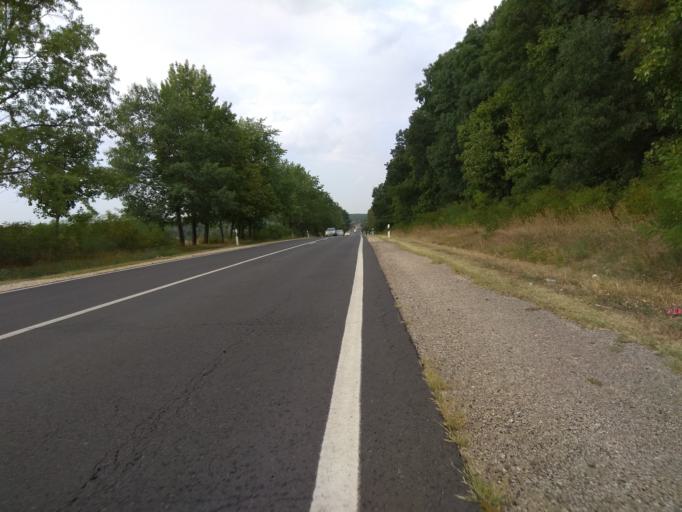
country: HU
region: Borsod-Abauj-Zemplen
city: Harsany
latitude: 47.9232
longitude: 20.7535
